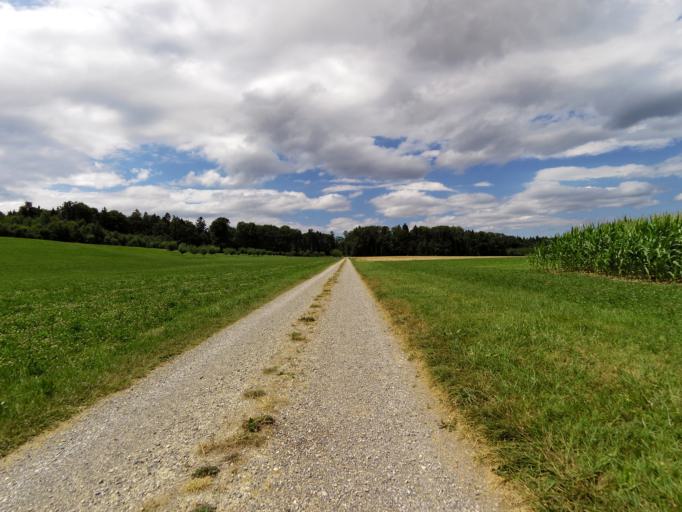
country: CH
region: Thurgau
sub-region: Kreuzlingen District
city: Ermatingen
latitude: 47.6513
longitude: 9.0832
